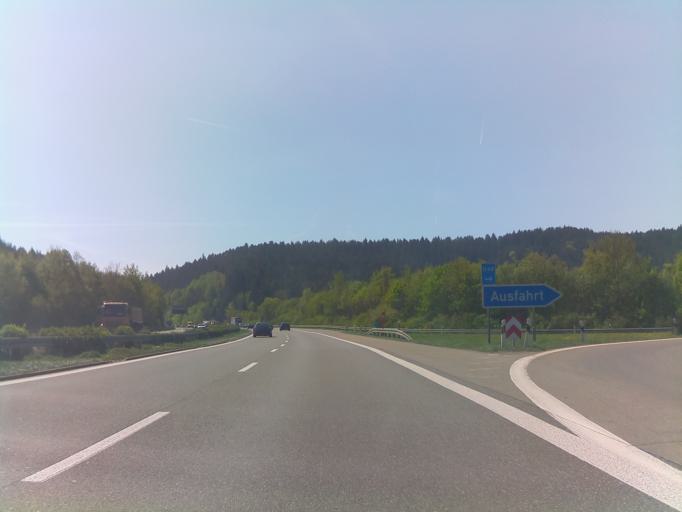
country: DE
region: Baden-Wuerttemberg
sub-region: Freiburg Region
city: Vohringen
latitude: 48.2984
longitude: 8.6348
